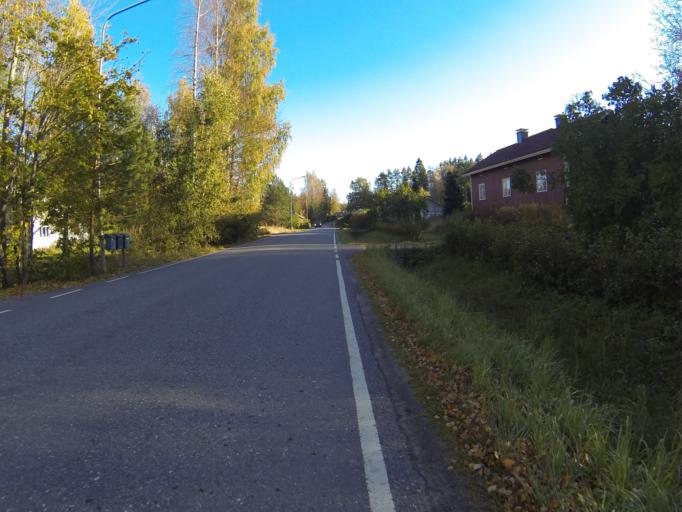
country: FI
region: Varsinais-Suomi
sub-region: Salo
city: Saerkisalo
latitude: 60.2139
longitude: 22.9180
